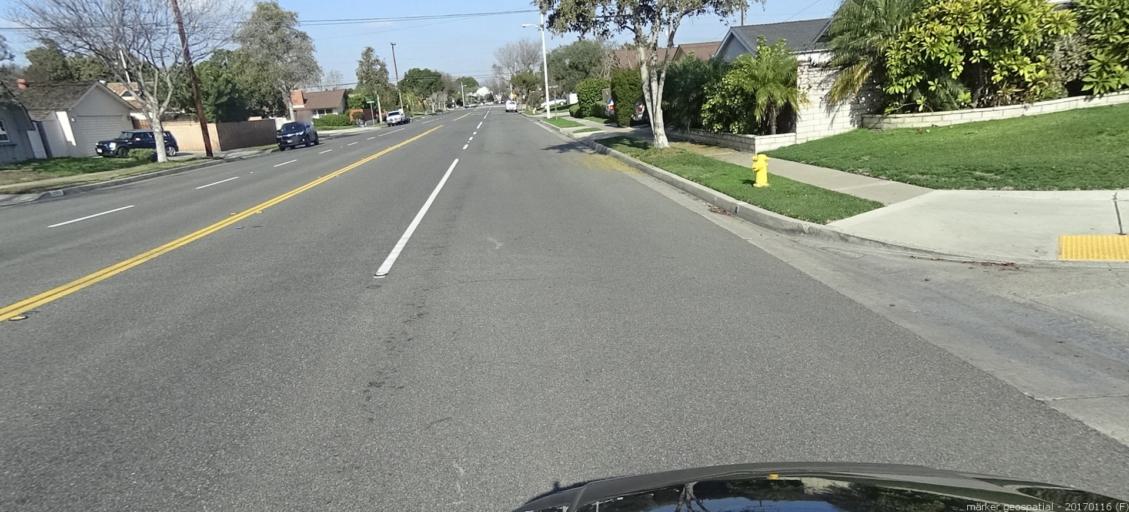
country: US
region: California
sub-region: Orange County
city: Rossmoor
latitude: 33.7888
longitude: -118.0764
